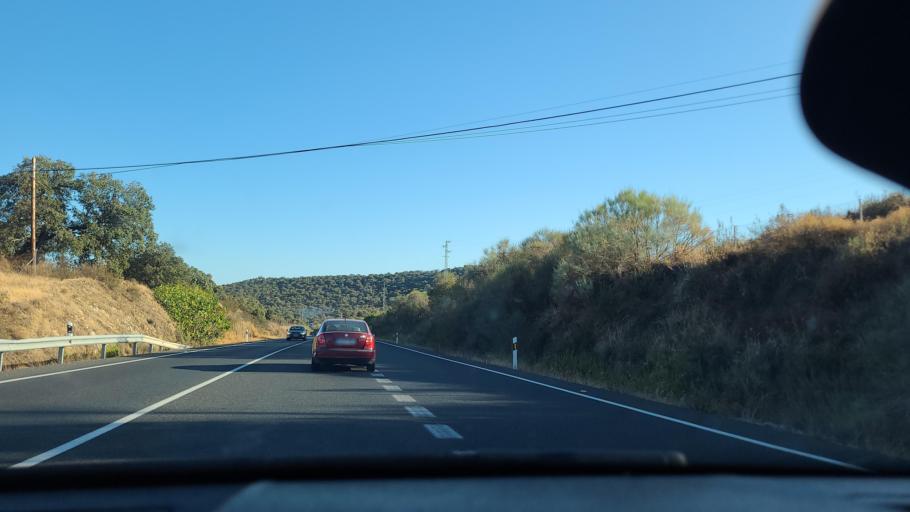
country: ES
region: Andalusia
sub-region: Province of Cordoba
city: Villaharta
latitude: 38.1076
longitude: -4.8795
